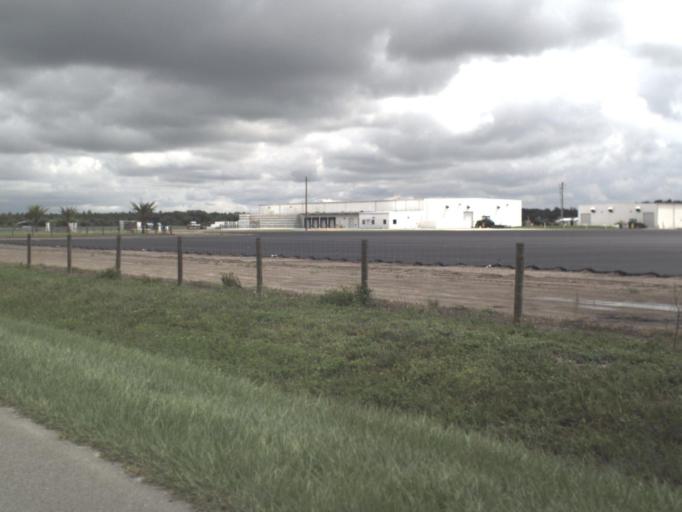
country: US
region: Florida
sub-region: Hillsborough County
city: Wimauma
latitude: 27.5871
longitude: -82.1610
